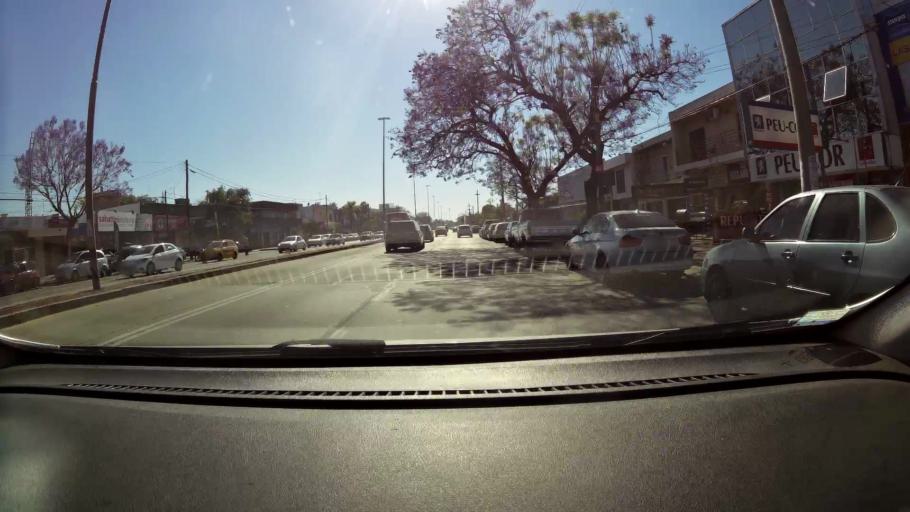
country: AR
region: Cordoba
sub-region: Departamento de Capital
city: Cordoba
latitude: -31.4332
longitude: -64.1560
